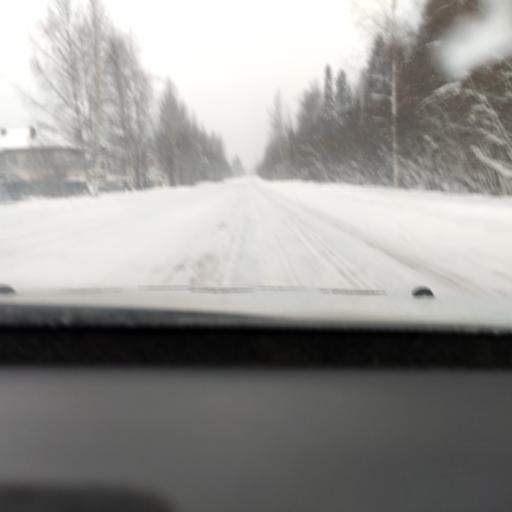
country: RU
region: Perm
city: Polazna
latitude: 58.1444
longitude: 56.4326
